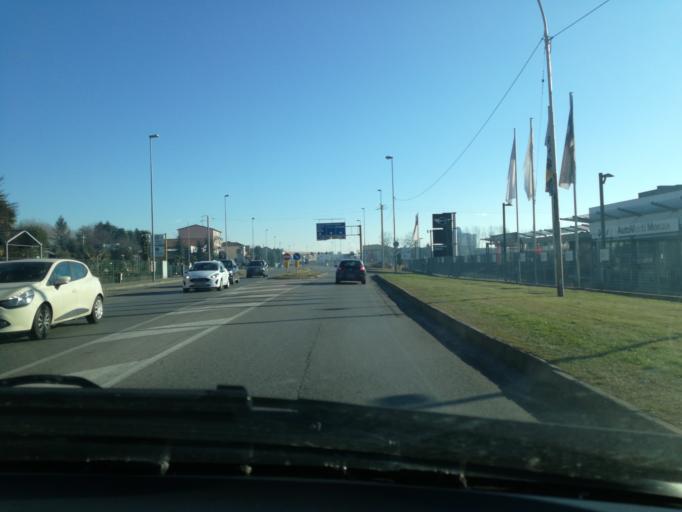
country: IT
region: Lombardy
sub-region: Provincia di Monza e Brianza
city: Concorezzo
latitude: 45.5802
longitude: 9.3207
